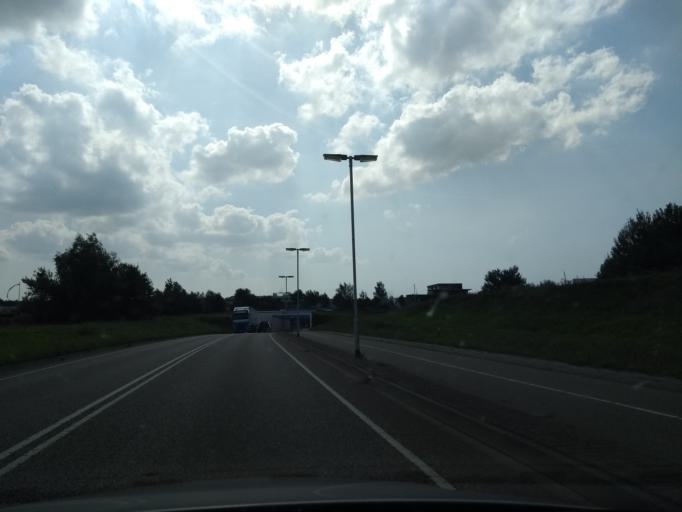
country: NL
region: Friesland
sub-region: Sudwest Fryslan
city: Oppenhuizen
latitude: 53.0279
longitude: 5.6848
